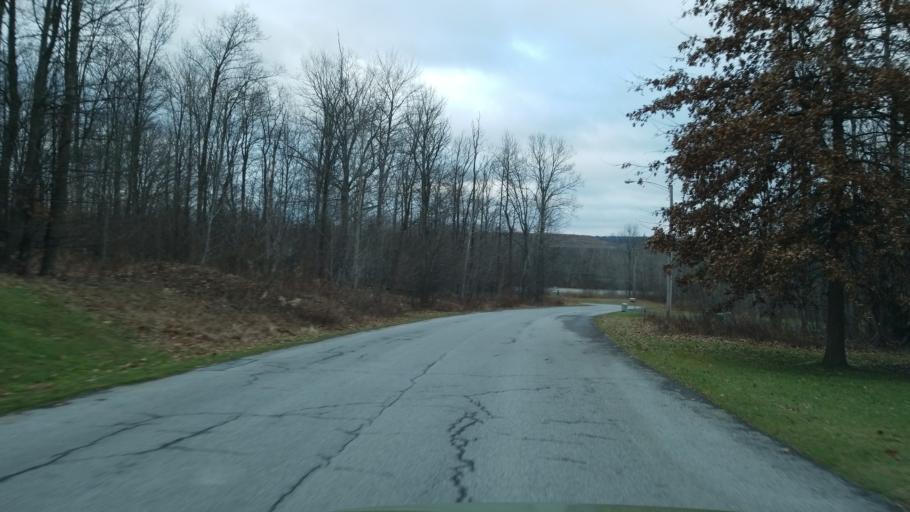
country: US
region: Pennsylvania
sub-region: Jefferson County
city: Falls Creek
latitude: 41.1367
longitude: -78.8084
